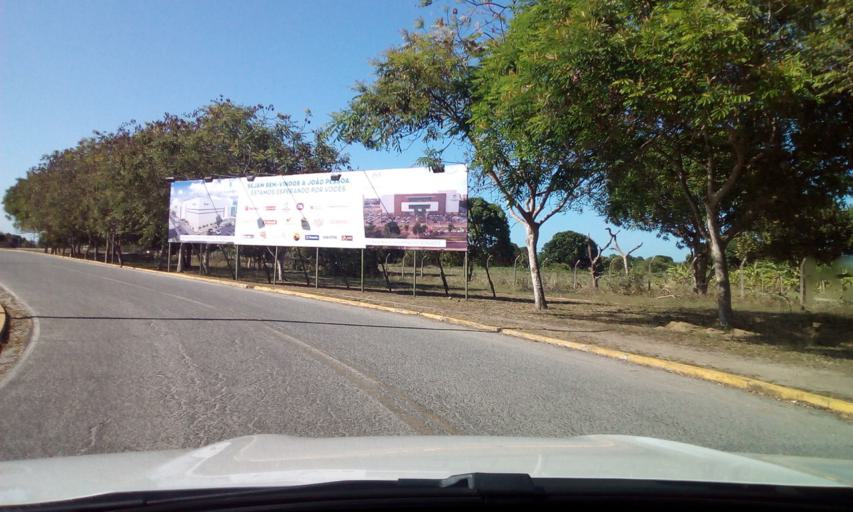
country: BR
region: Paraiba
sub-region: Bayeux
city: Bayeux
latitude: -7.1460
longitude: -34.9466
